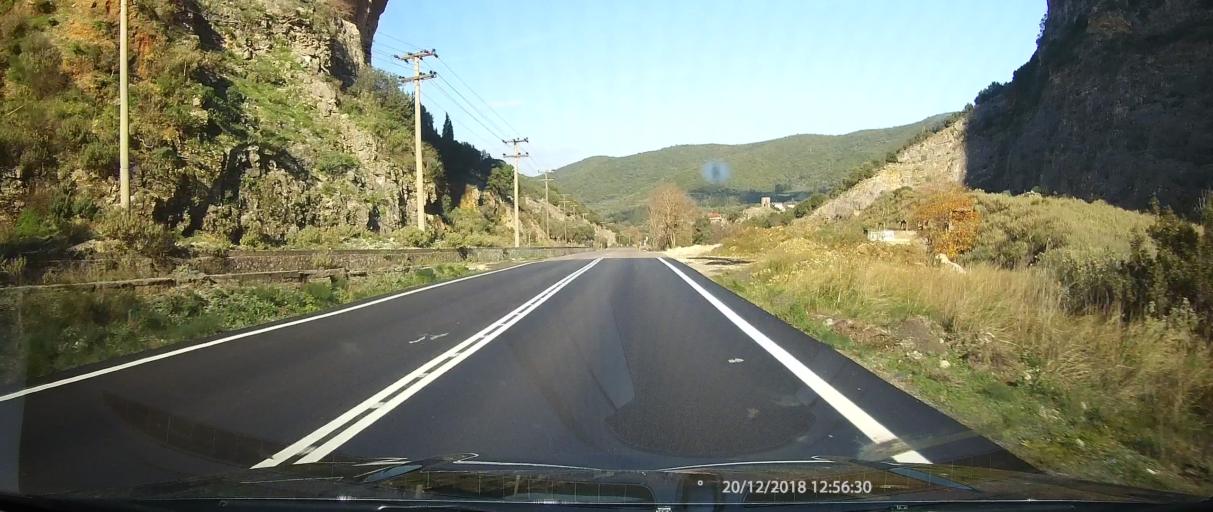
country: GR
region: West Greece
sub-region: Nomos Aitolias kai Akarnanias
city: Pappadhatai
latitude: 38.5116
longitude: 21.3793
